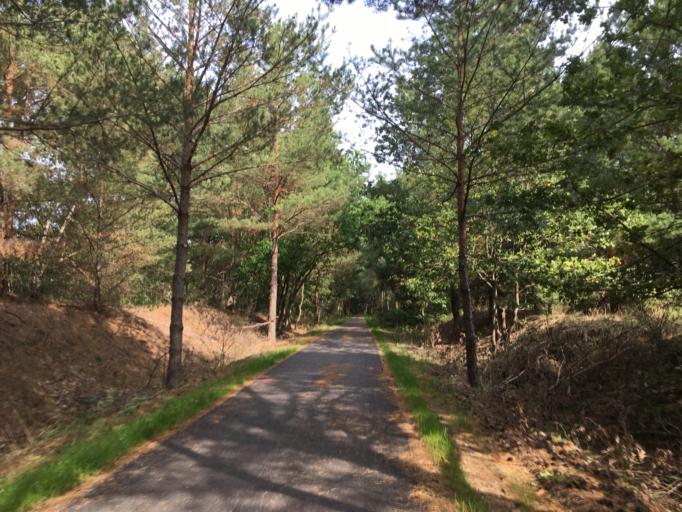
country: DE
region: Brandenburg
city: Heinersbruck
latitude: 51.8301
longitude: 14.5852
